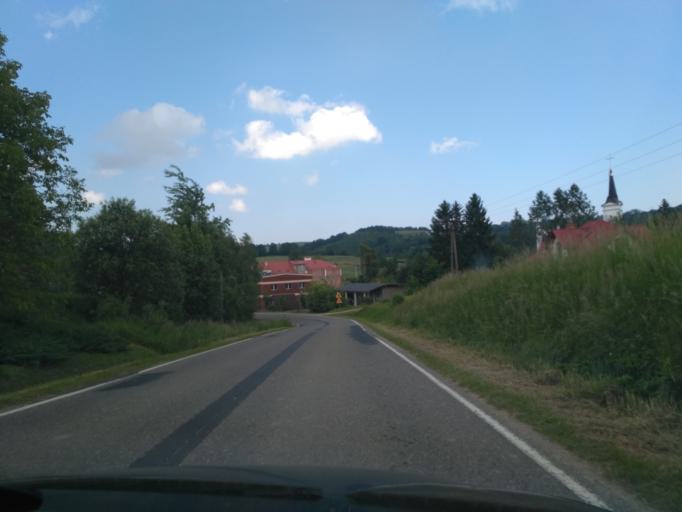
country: PL
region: Subcarpathian Voivodeship
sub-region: Powiat rzeszowski
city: Hyzne
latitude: 49.9525
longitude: 22.2027
